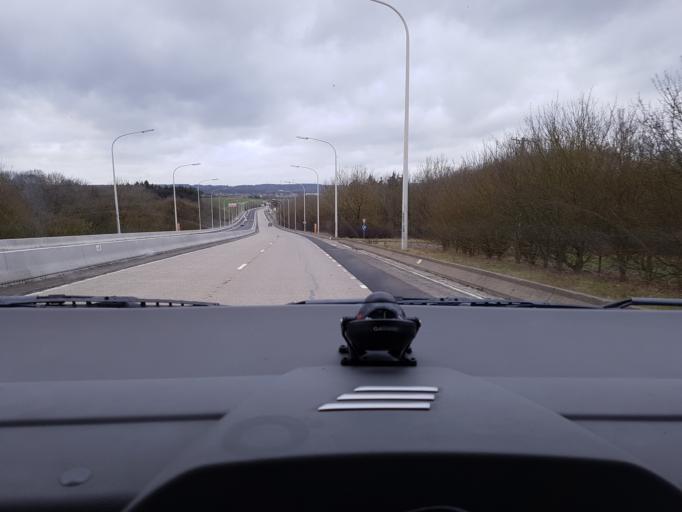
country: BE
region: Wallonia
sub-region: Province du Luxembourg
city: Marche-en-Famenne
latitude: 50.2619
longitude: 5.2590
